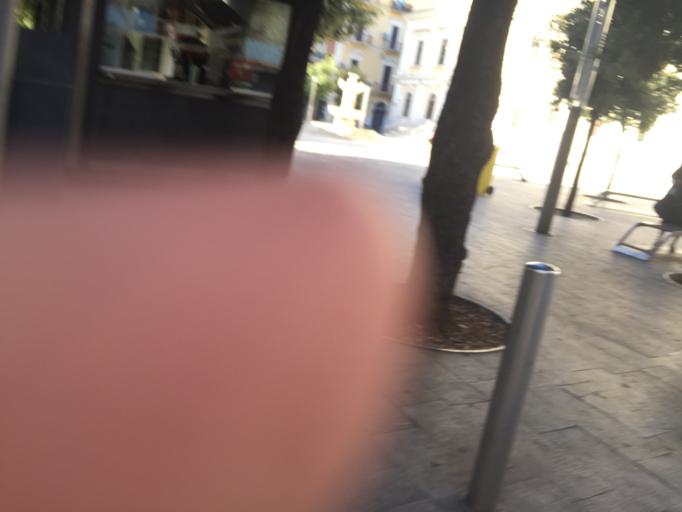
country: IT
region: Apulia
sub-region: Provincia di Bari
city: Bari
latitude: 41.1231
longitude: 16.8610
